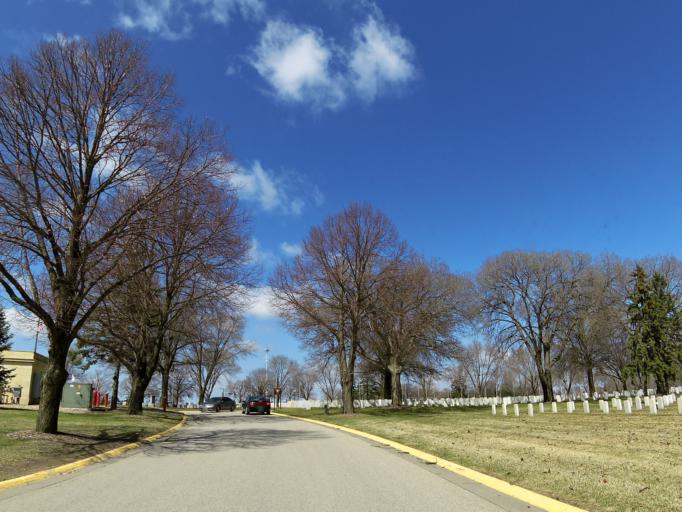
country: US
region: Minnesota
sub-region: Hennepin County
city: Richfield
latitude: 44.8654
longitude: -93.2211
